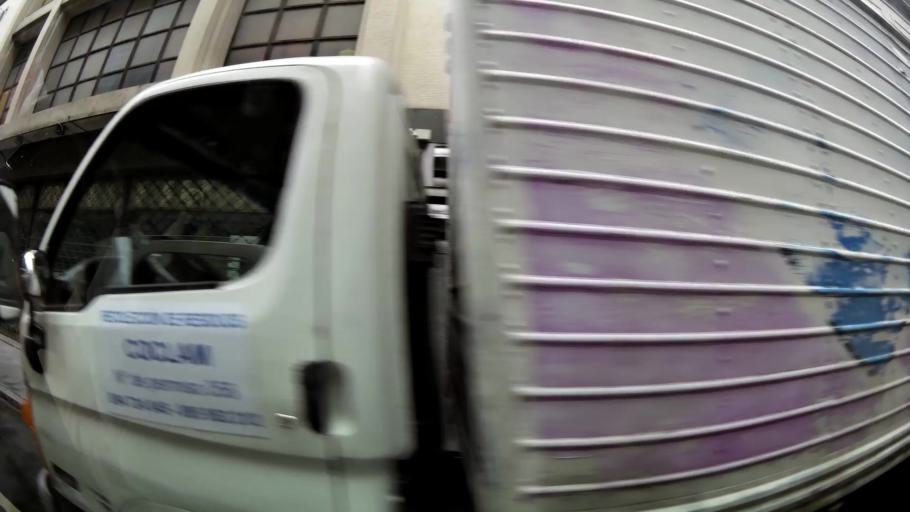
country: UY
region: Montevideo
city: Montevideo
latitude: -34.9075
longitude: -56.2070
